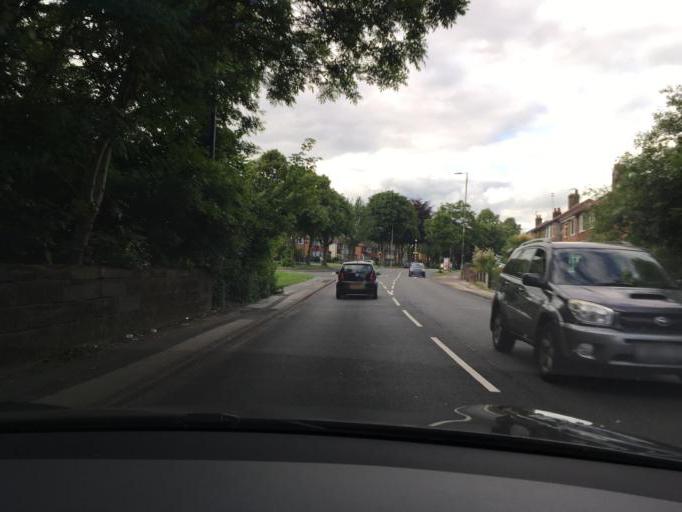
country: GB
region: England
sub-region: Trafford
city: Urmston
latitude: 53.4593
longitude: -2.3580
